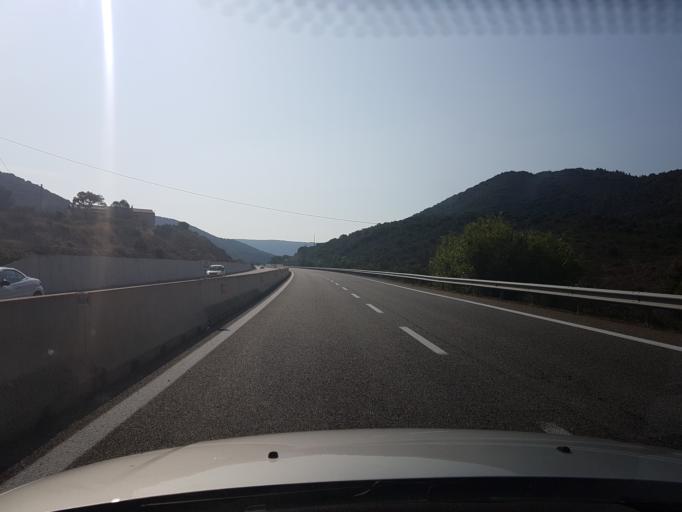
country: IT
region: Sardinia
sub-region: Provincia di Olbia-Tempio
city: Loiri Porto San Paolo
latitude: 40.8333
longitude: 9.5609
